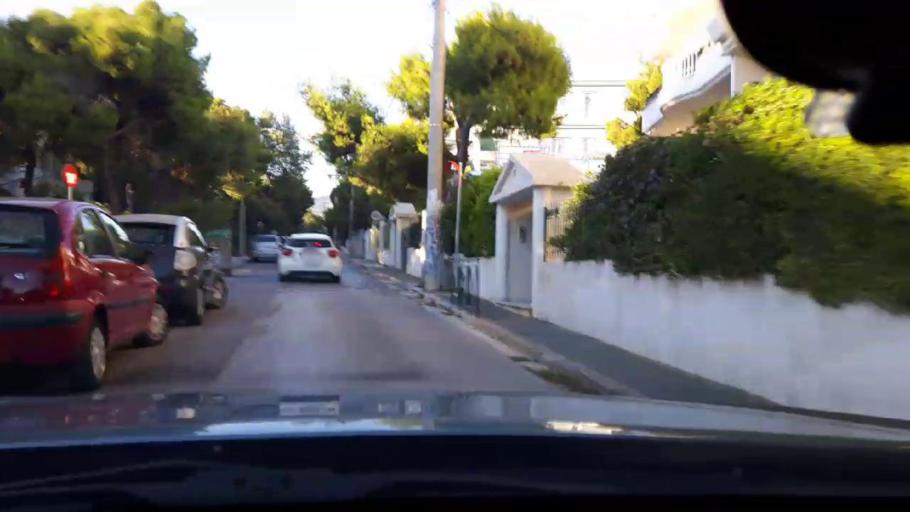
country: GR
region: Attica
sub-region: Nomarchia Athinas
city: Melissia
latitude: 38.0485
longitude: 23.8335
